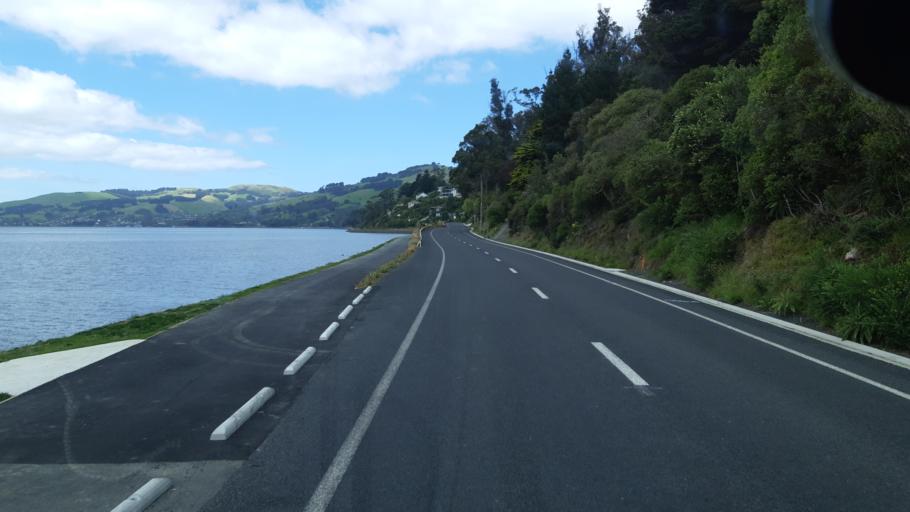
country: NZ
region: Otago
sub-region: Dunedin City
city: Dunedin
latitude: -45.8793
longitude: 170.5429
